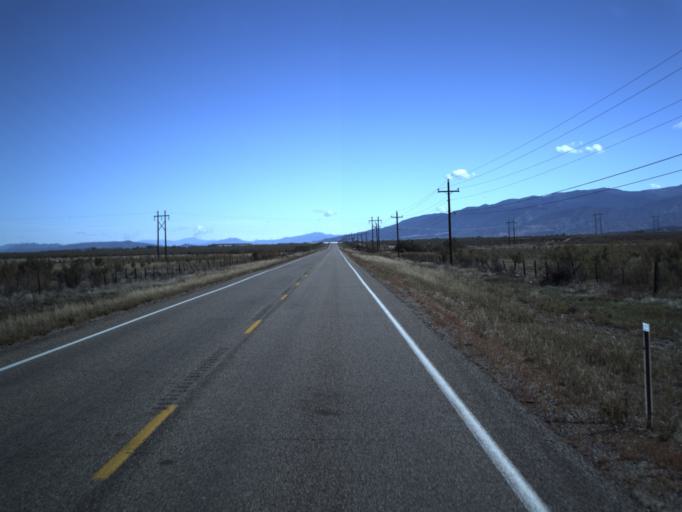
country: US
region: Utah
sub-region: Iron County
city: Cedar City
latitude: 37.6610
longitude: -113.2114
